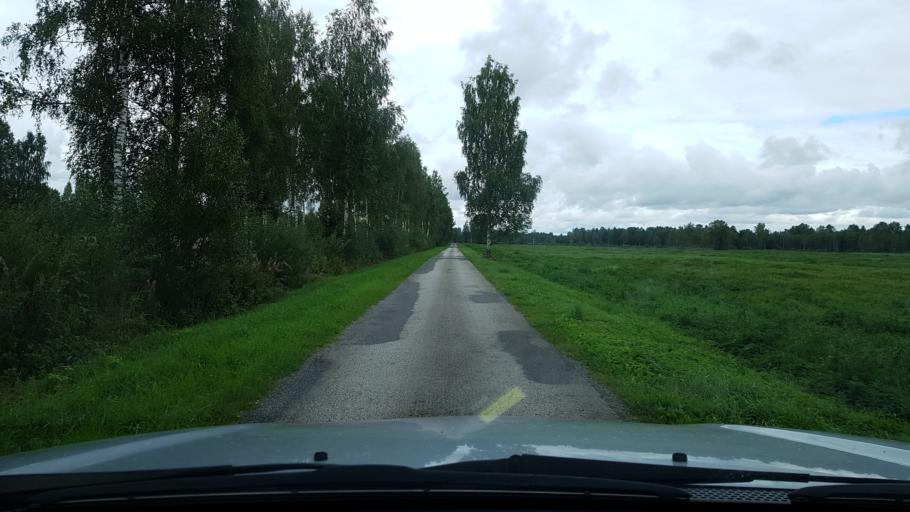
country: EE
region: Harju
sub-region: Raasiku vald
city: Arukula
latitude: 59.2970
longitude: 25.0567
